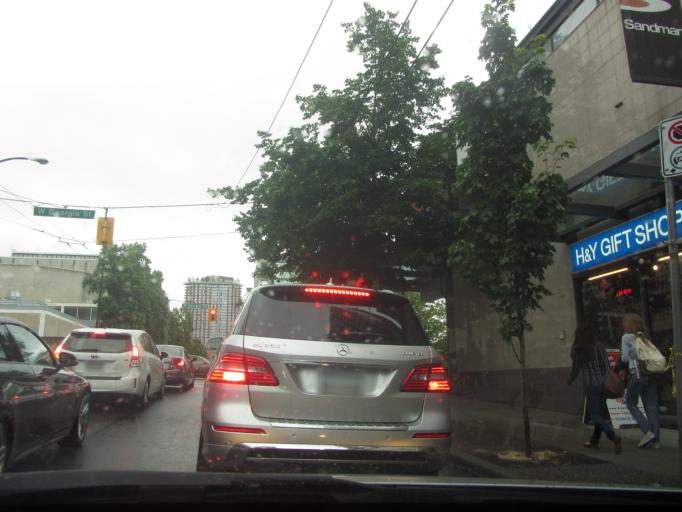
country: CA
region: British Columbia
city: West End
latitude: 49.2791
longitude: -123.1136
